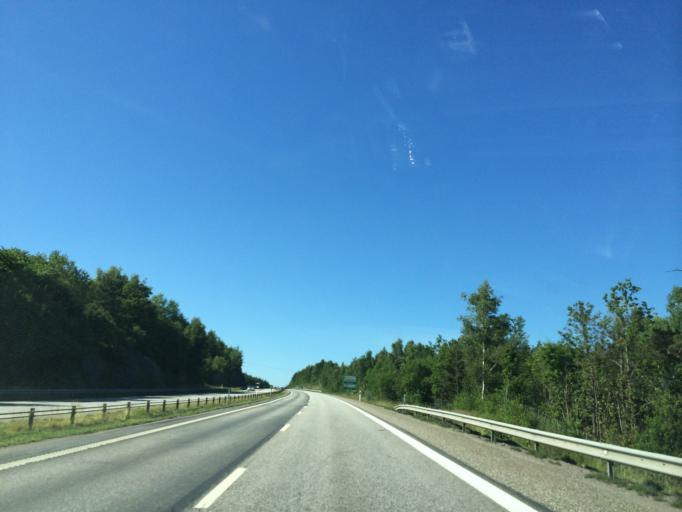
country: SE
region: Joenkoeping
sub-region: Jonkopings Kommun
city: Kaxholmen
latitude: 57.9583
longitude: 14.3515
